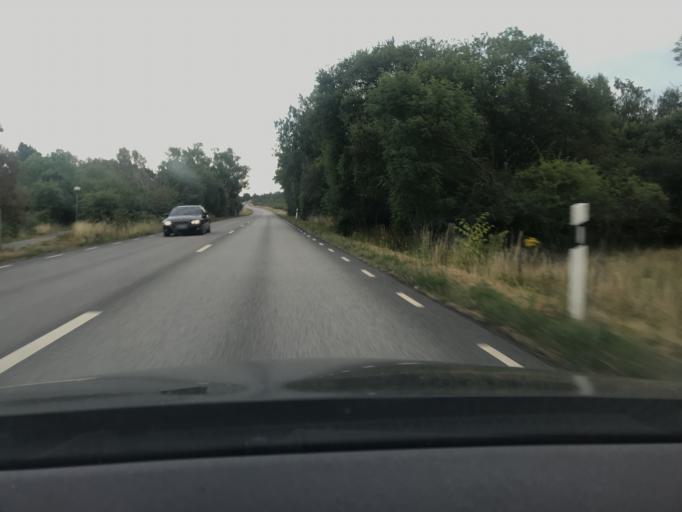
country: SE
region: Skane
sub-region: Simrishamns Kommun
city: Simrishamn
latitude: 55.5846
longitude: 14.3255
